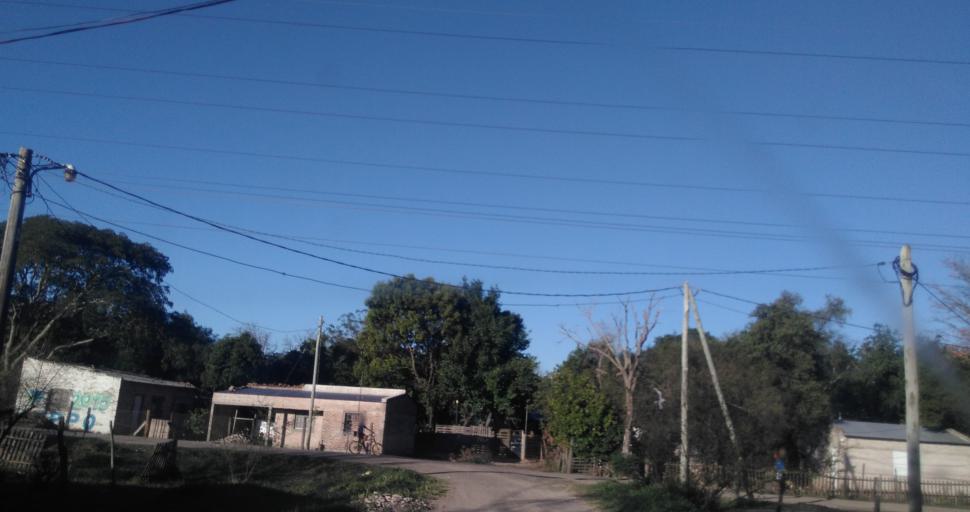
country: AR
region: Chaco
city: Resistencia
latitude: -27.4258
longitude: -58.9725
